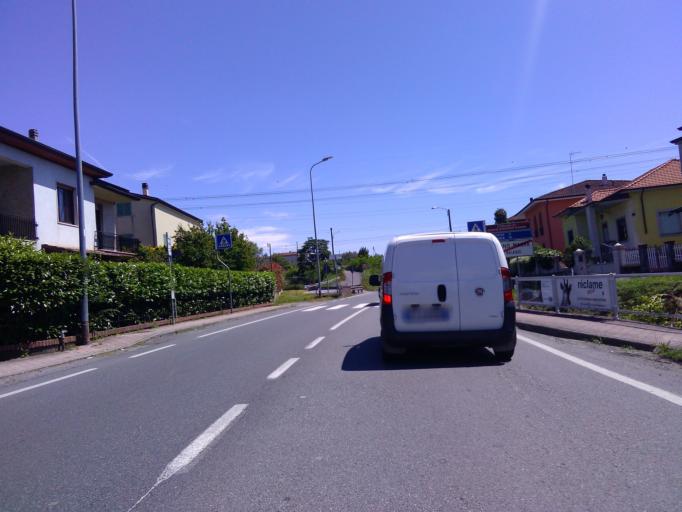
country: IT
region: Liguria
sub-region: Provincia di La Spezia
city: Santo Stefano di Magra
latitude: 44.1322
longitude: 9.9403
